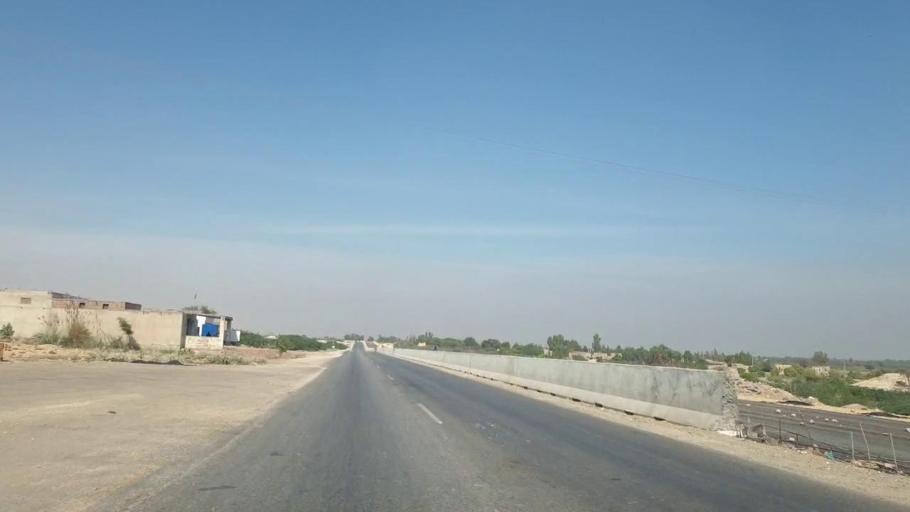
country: PK
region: Sindh
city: Hala
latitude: 25.7057
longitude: 68.2958
